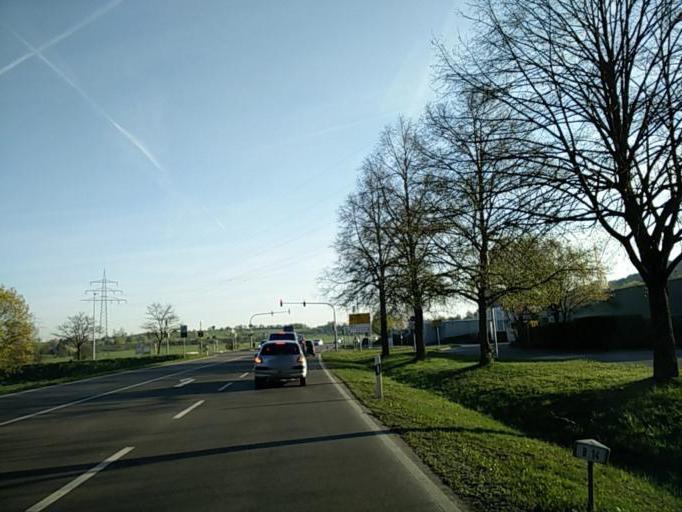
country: DE
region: Baden-Wuerttemberg
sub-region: Regierungsbezirk Stuttgart
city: Herrenberg
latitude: 48.6039
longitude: 8.8740
